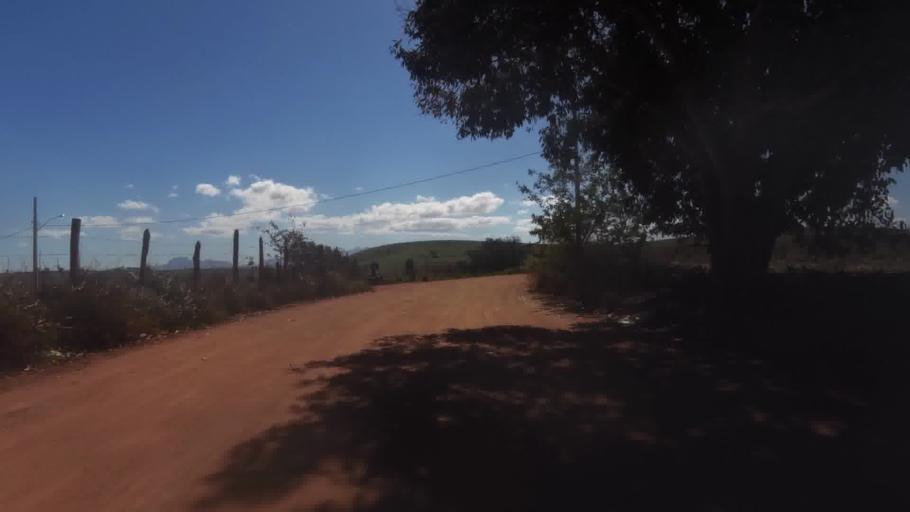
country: BR
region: Espirito Santo
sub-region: Marataizes
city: Marataizes
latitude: -21.1384
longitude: -40.9928
